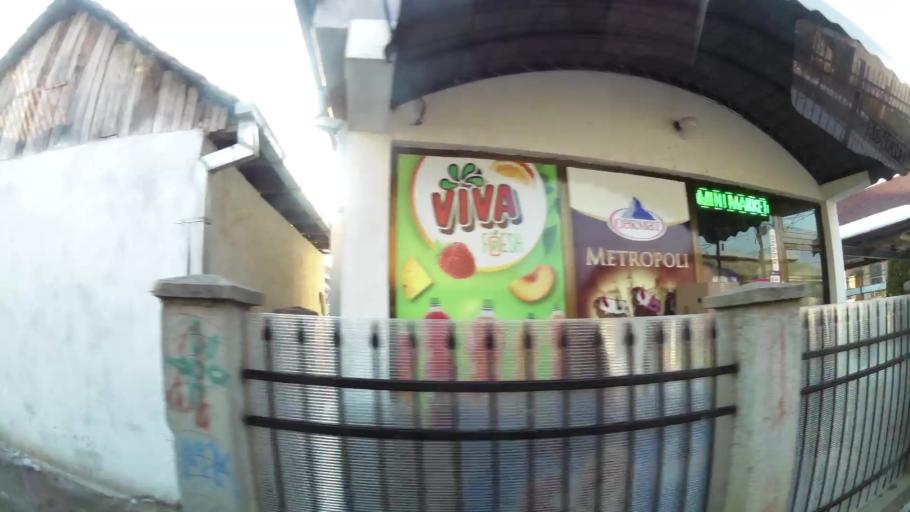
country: MK
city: Creshevo
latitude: 42.0229
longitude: 21.5205
